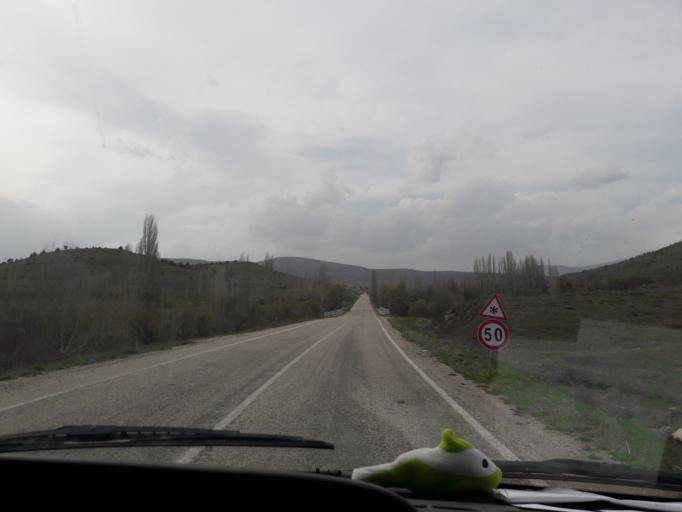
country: TR
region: Gumushane
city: Siran
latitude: 40.1635
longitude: 39.0083
